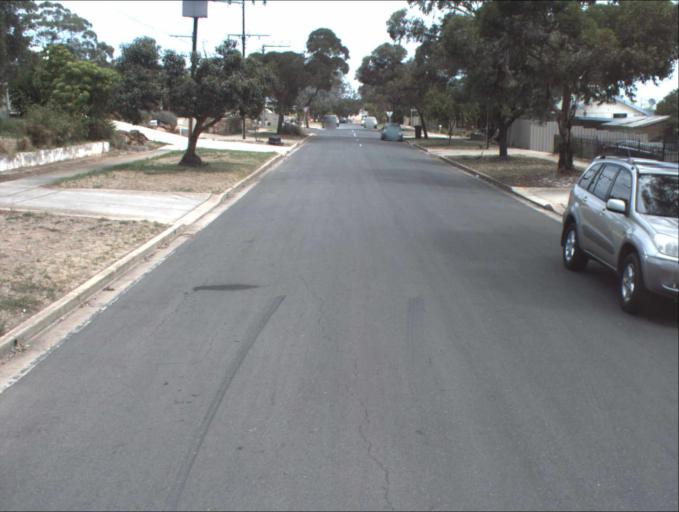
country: AU
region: South Australia
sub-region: Port Adelaide Enfield
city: Enfield
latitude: -34.8491
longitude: 138.6104
